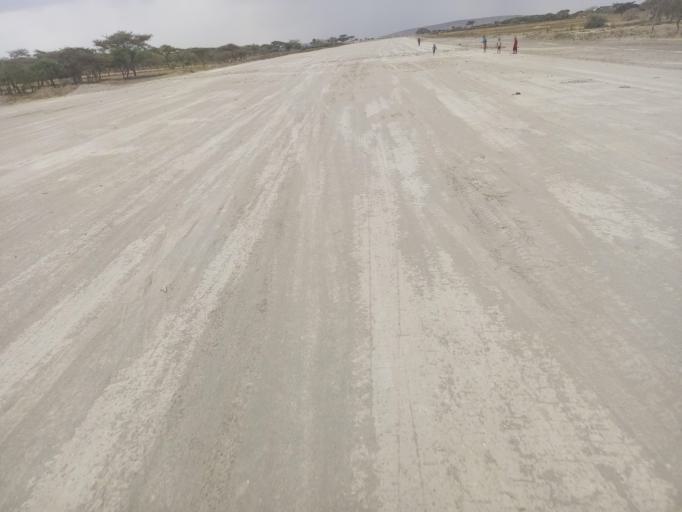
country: ET
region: Oromiya
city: Ziway
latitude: 7.8548
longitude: 38.6660
